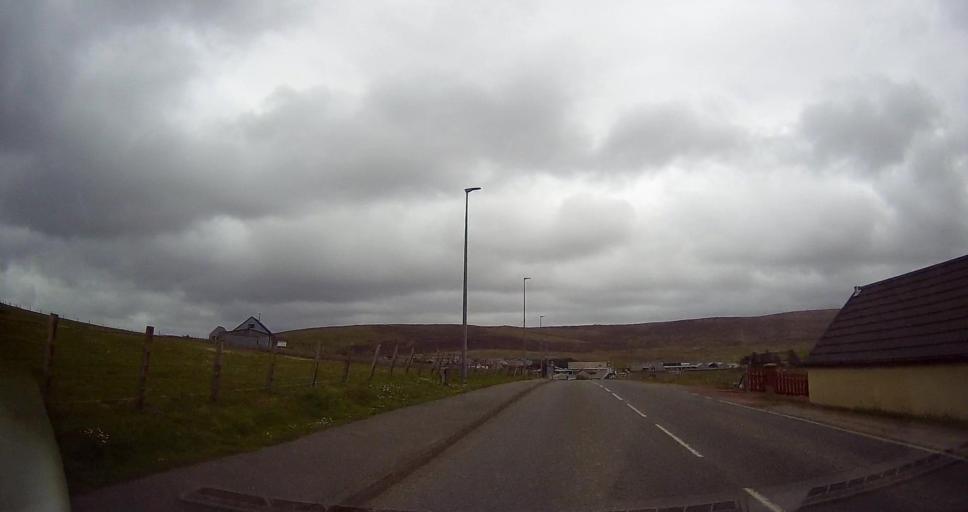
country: GB
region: Scotland
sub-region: Shetland Islands
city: Lerwick
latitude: 60.3940
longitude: -1.3610
